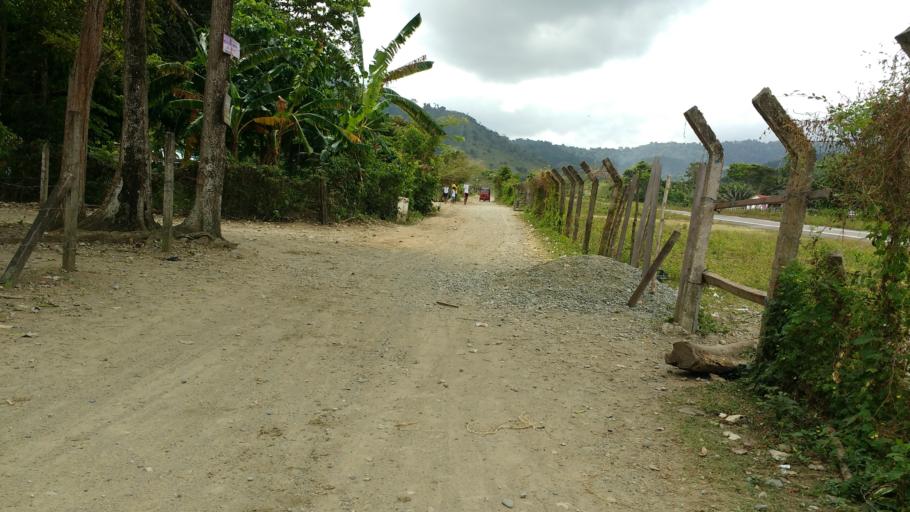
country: PA
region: Guna Yala
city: Puerto Obaldia
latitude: 8.6333
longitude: -77.3492
